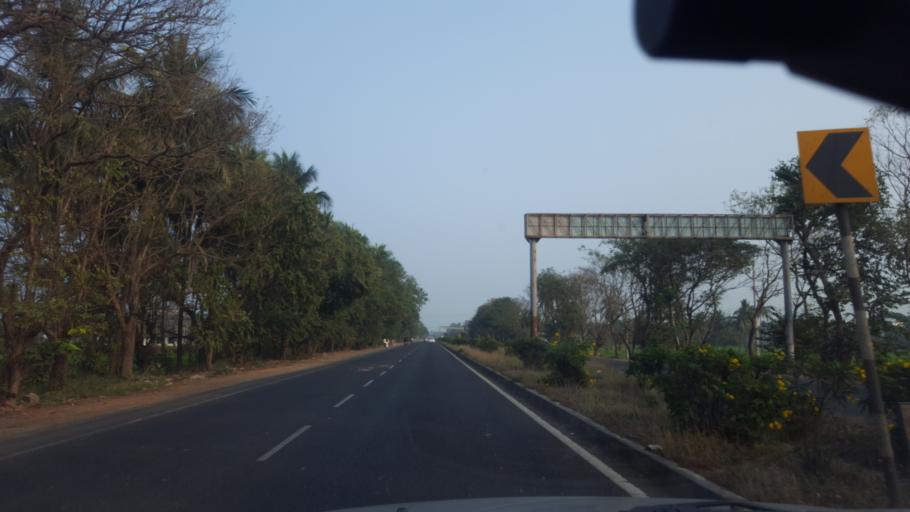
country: IN
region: Andhra Pradesh
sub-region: West Godavari
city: Tadepallegudem
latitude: 16.8077
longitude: 81.5782
